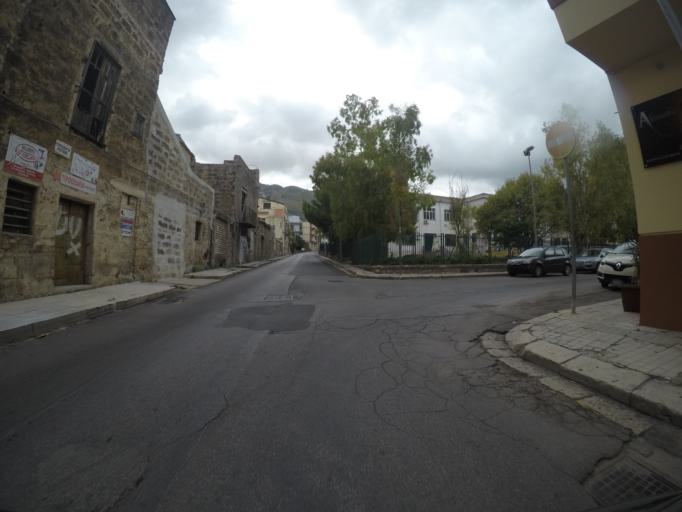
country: IT
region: Sicily
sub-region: Palermo
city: Carini
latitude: 38.1362
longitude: 13.1874
